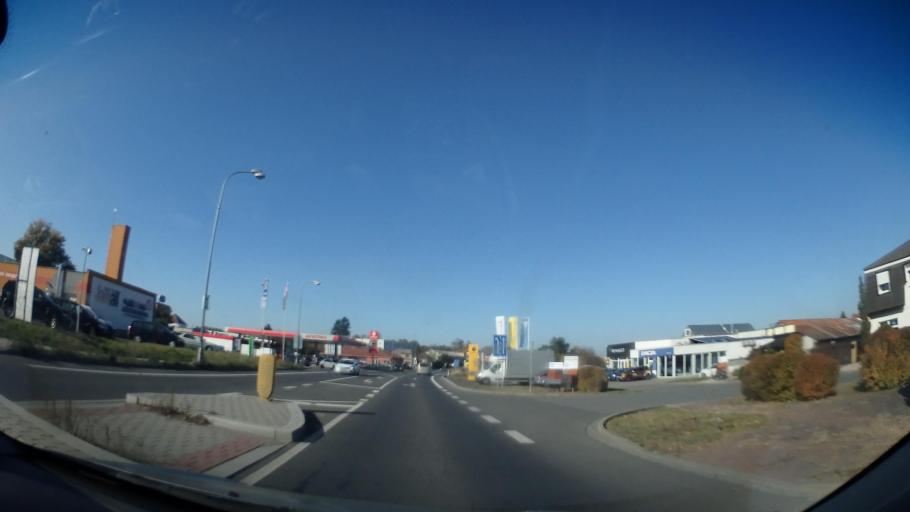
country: CZ
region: Pardubicky
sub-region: Okres Chrudim
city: Chrudim
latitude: 49.9367
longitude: 15.7966
